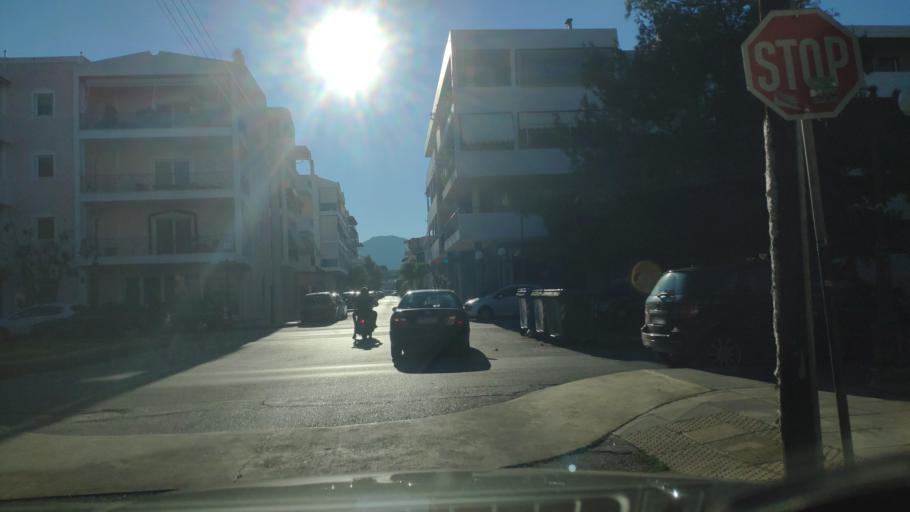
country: GR
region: Peloponnese
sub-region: Nomos Korinthias
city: Korinthos
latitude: 37.9372
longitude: 22.9243
